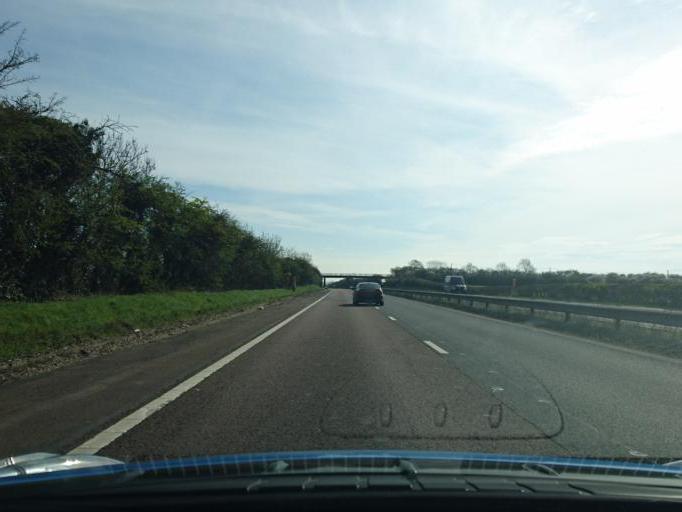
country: GB
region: England
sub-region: Herefordshire
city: Donnington
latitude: 51.9957
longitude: -2.3159
